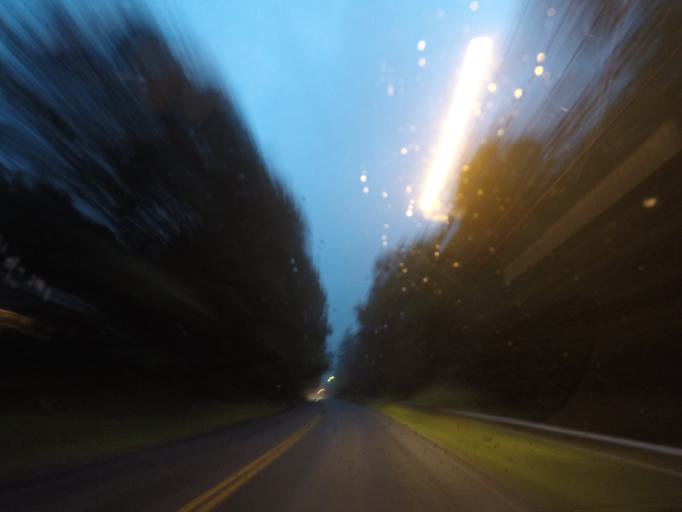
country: US
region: Massachusetts
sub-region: Worcester County
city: Southbridge
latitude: 42.0727
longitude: -72.0587
